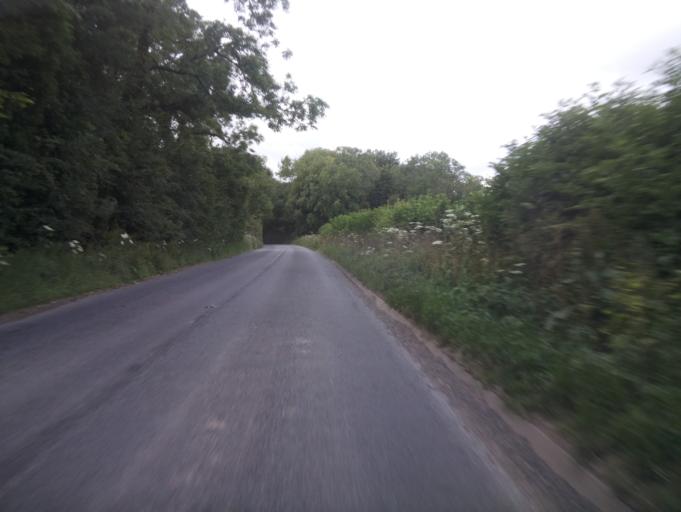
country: GB
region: England
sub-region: Gloucestershire
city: Chipping Campden
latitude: 52.0004
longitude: -1.7574
